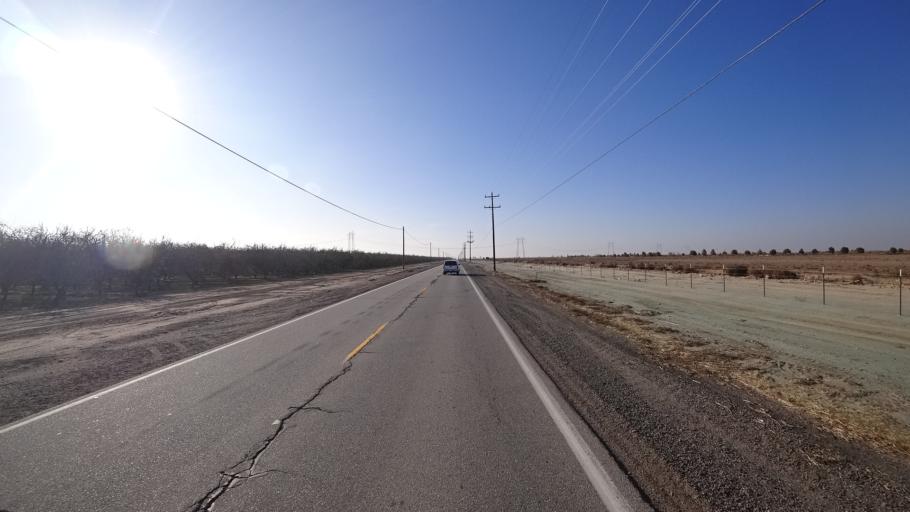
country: US
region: California
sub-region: Kern County
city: Rosedale
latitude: 35.2962
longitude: -119.1650
